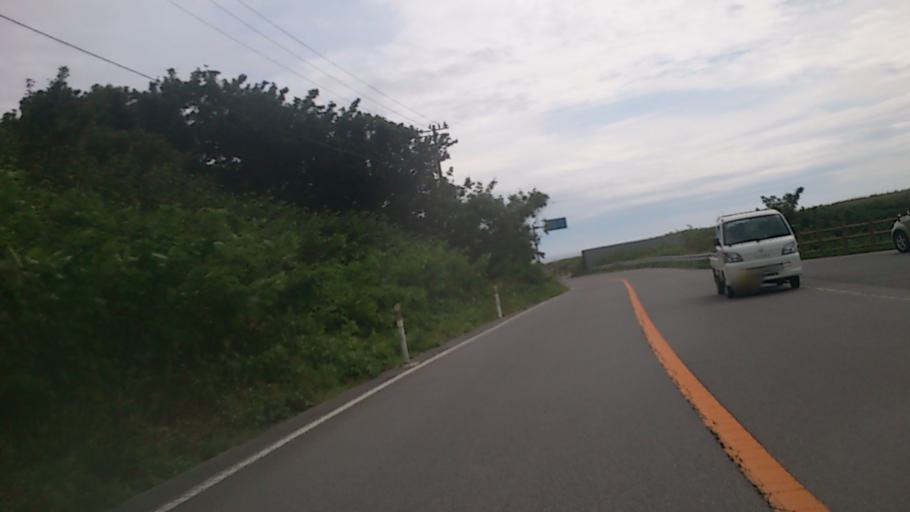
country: JP
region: Akita
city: Noshiromachi
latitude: 40.4302
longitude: 139.9413
